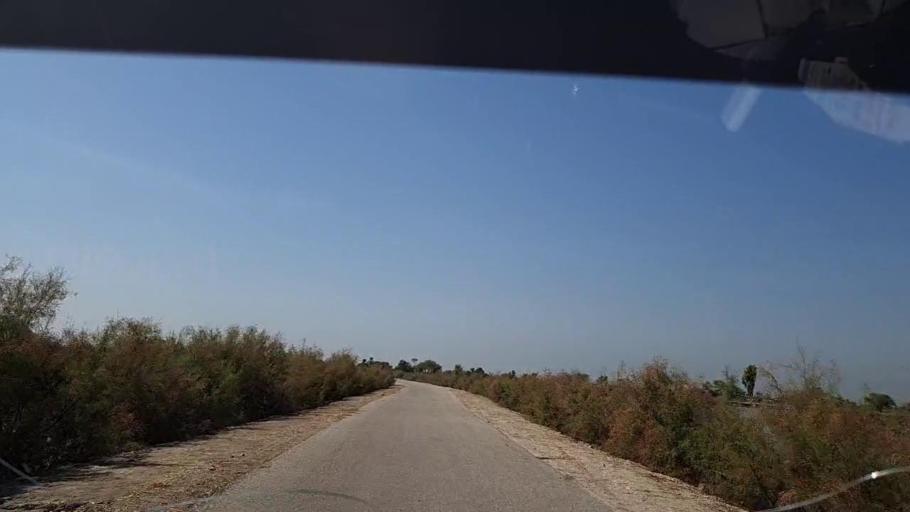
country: PK
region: Sindh
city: Tangwani
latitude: 28.3140
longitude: 69.0978
